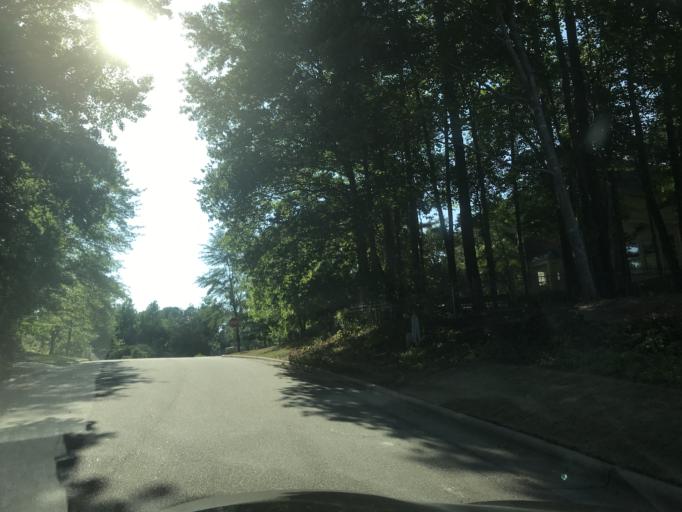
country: US
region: North Carolina
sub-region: Wake County
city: West Raleigh
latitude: 35.8833
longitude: -78.6043
